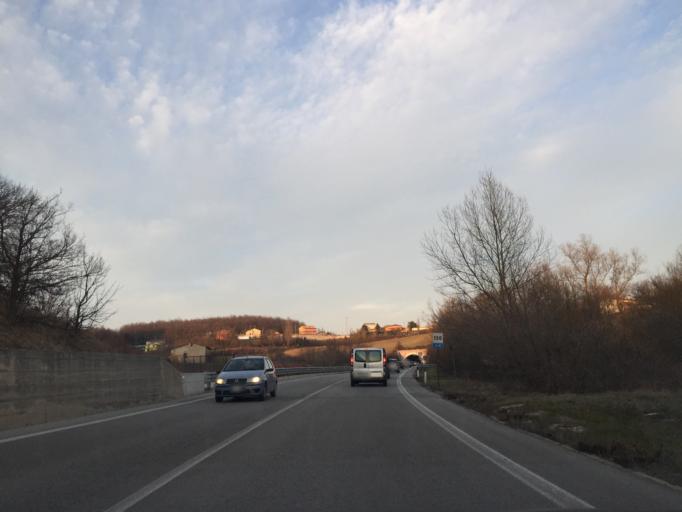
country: IT
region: Molise
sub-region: Provincia di Campobasso
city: Mimosa-Poggio Verde-Nuova Comunita
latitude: 41.5442
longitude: 14.6241
